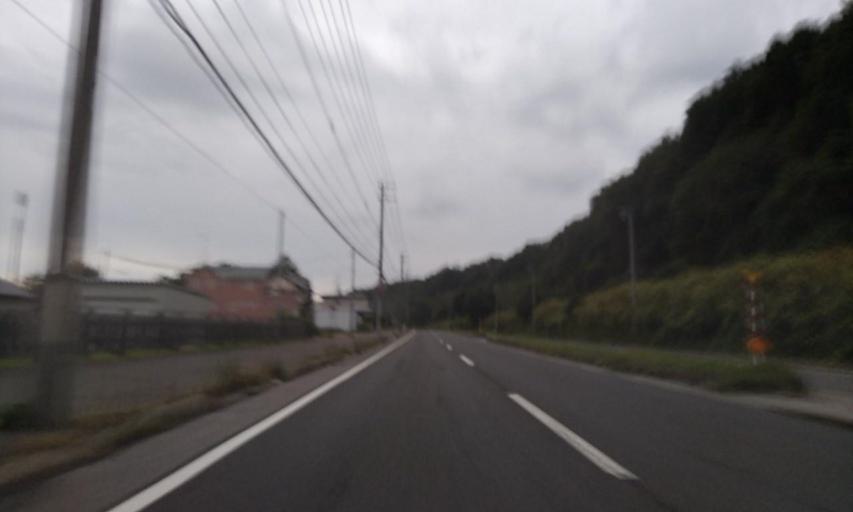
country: JP
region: Hokkaido
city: Abashiri
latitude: 43.9862
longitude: 144.2952
